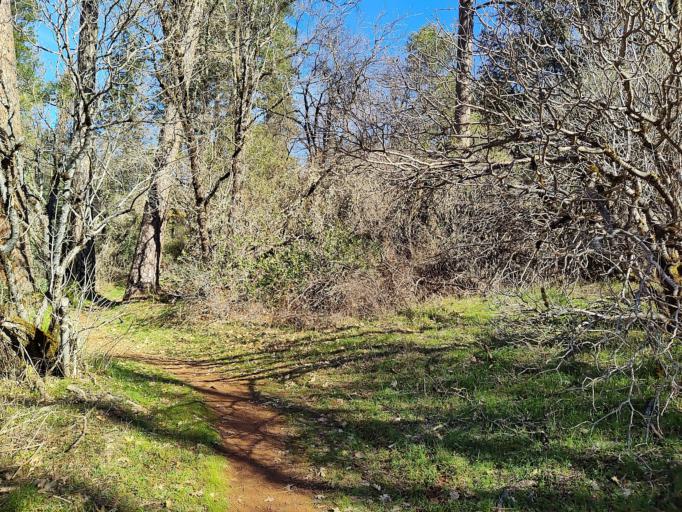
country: US
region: California
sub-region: Placer County
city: Meadow Vista
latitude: 39.0273
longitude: -120.9863
